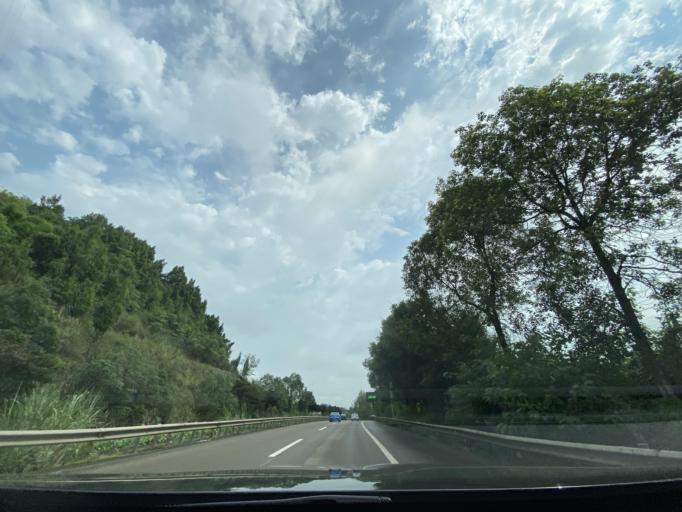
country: CN
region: Sichuan
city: Yanjiang
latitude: 29.9364
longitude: 104.6193
